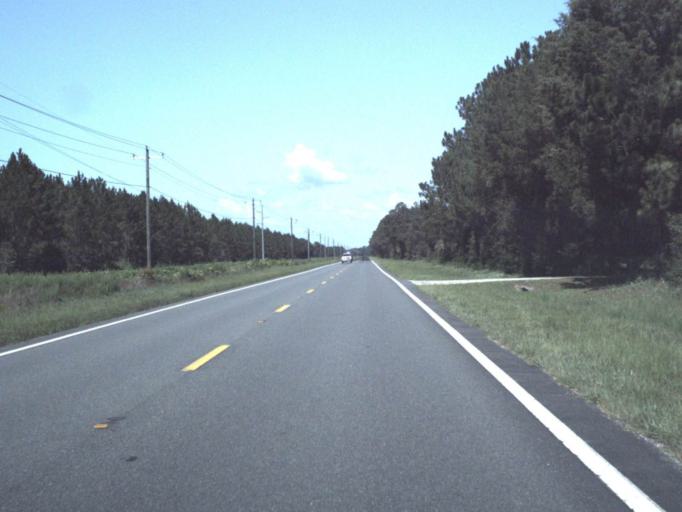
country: US
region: Florida
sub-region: Levy County
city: Chiefland
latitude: 29.2409
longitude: -82.9278
